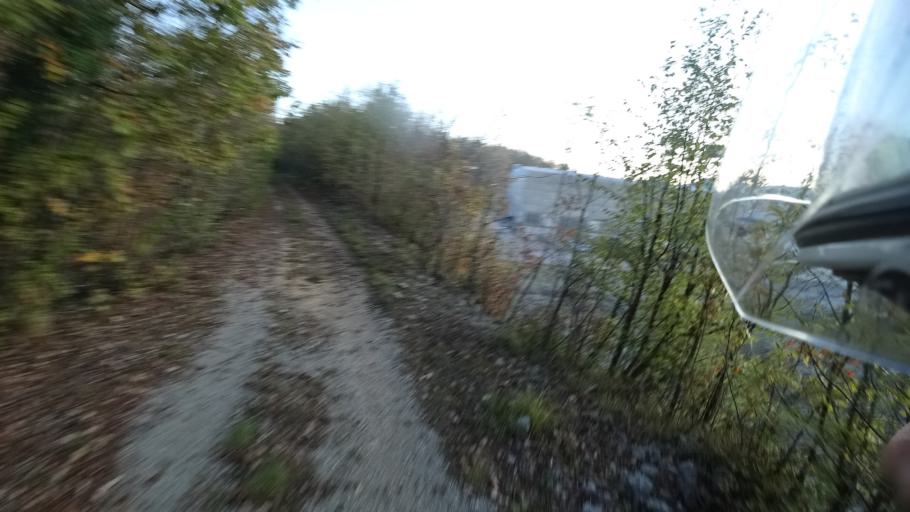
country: HR
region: Primorsko-Goranska
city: Matulji
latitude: 45.4055
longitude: 14.3094
